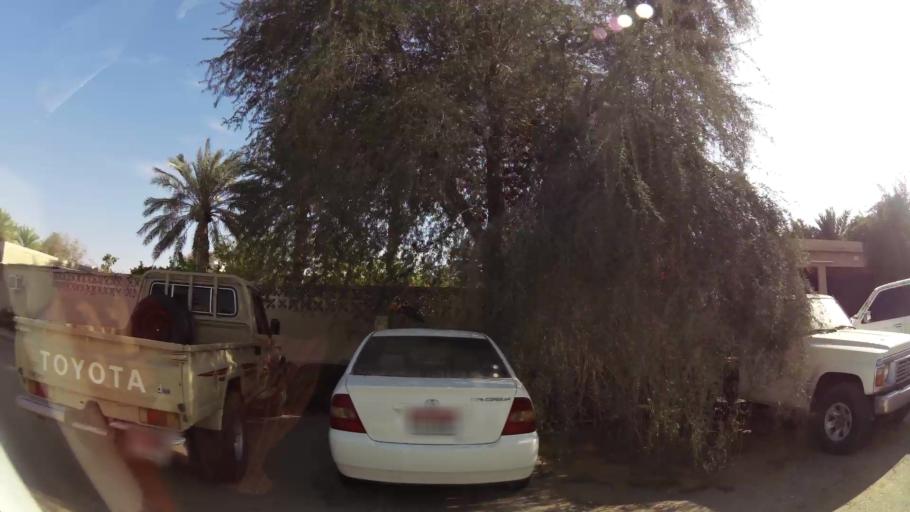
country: AE
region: Abu Dhabi
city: Al Ain
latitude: 24.0422
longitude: 55.8441
